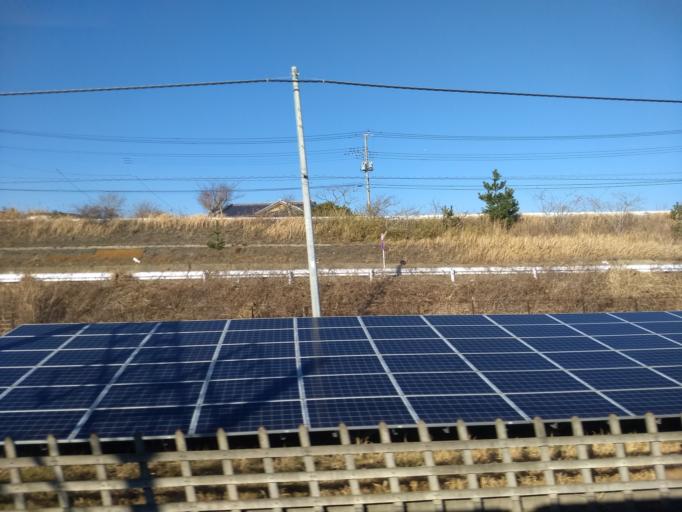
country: JP
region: Chiba
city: Shiroi
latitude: 35.8059
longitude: 140.1464
